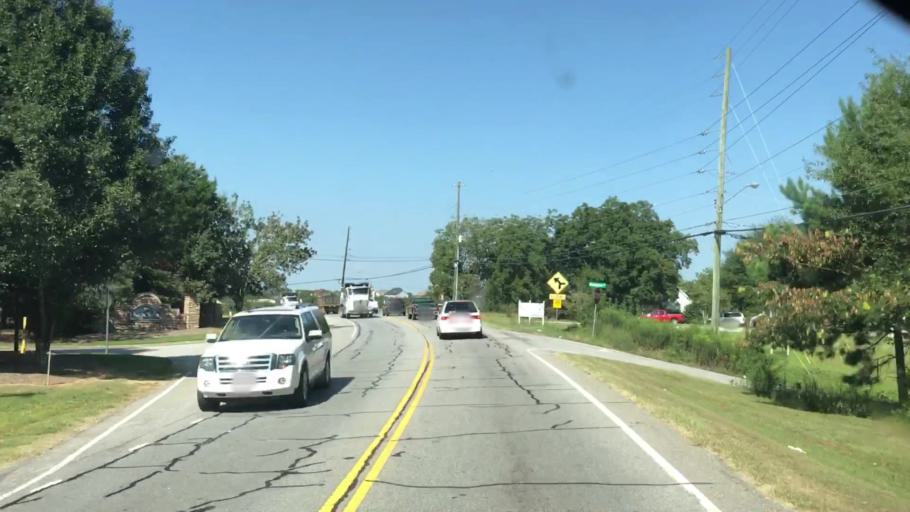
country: US
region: Georgia
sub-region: Walton County
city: Loganville
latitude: 33.8544
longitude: -83.8874
